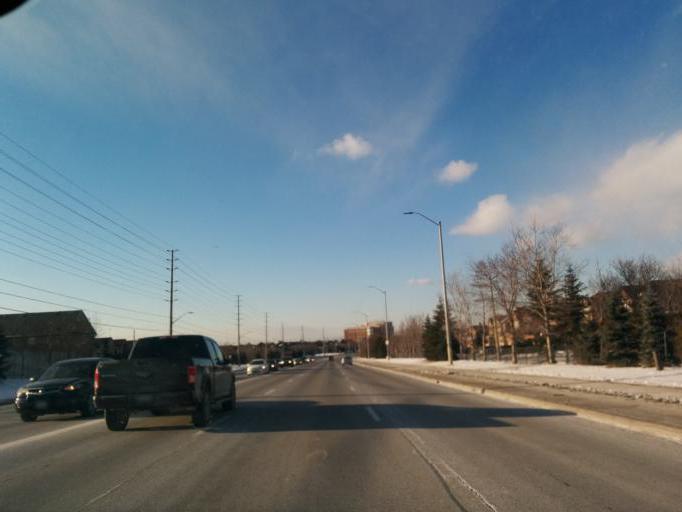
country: CA
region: Ontario
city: Mississauga
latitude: 43.6003
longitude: -79.6824
